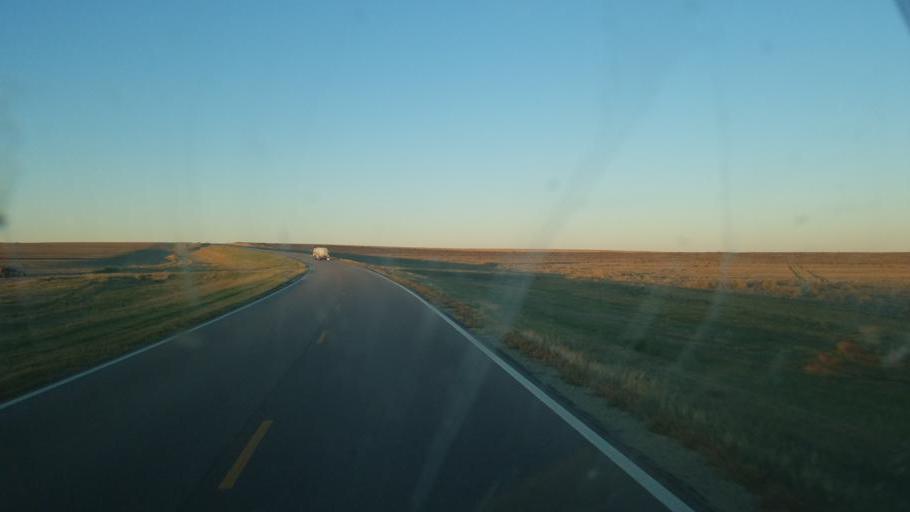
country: US
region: Kansas
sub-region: Wallace County
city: Sharon Springs
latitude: 38.8998
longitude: -101.8621
